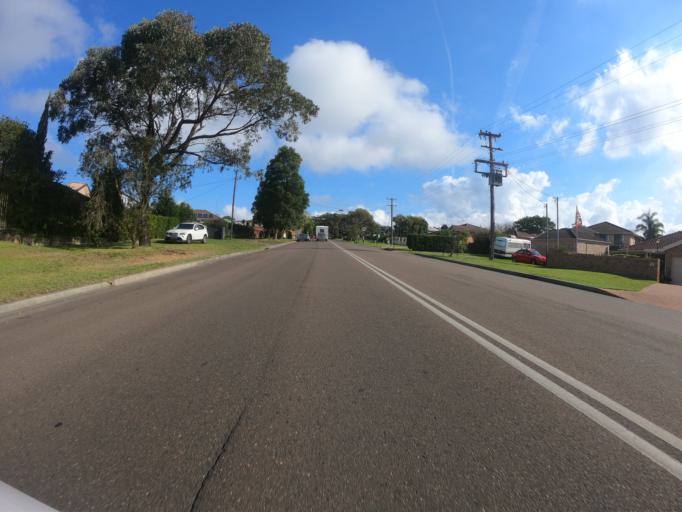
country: AU
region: New South Wales
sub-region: Wollongong
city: Helensburgh
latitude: -34.1943
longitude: 150.9762
